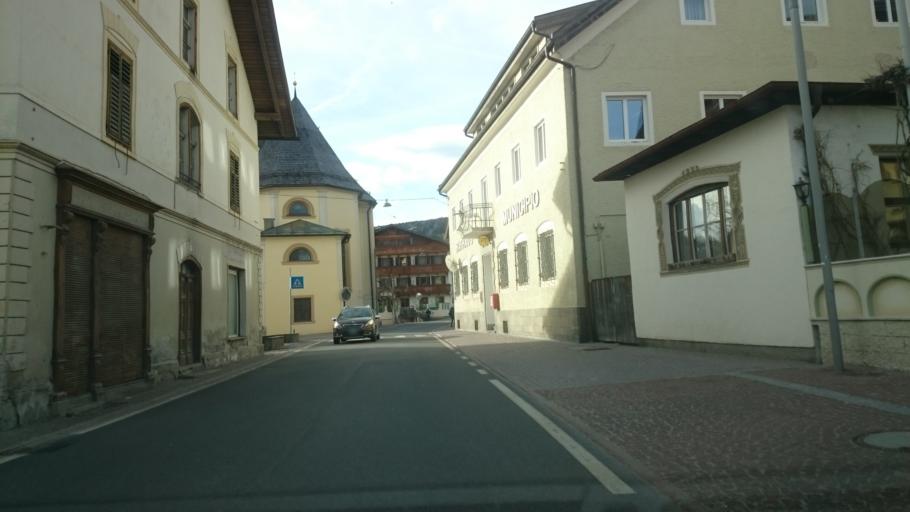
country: IT
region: Trentino-Alto Adige
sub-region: Bolzano
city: Monguelfo
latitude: 46.7566
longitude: 12.1050
